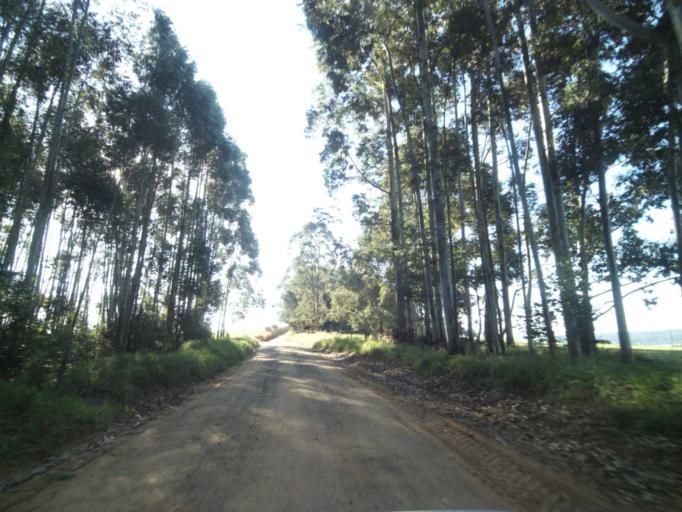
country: BR
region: Parana
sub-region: Tibagi
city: Tibagi
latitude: -24.5410
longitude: -50.6243
